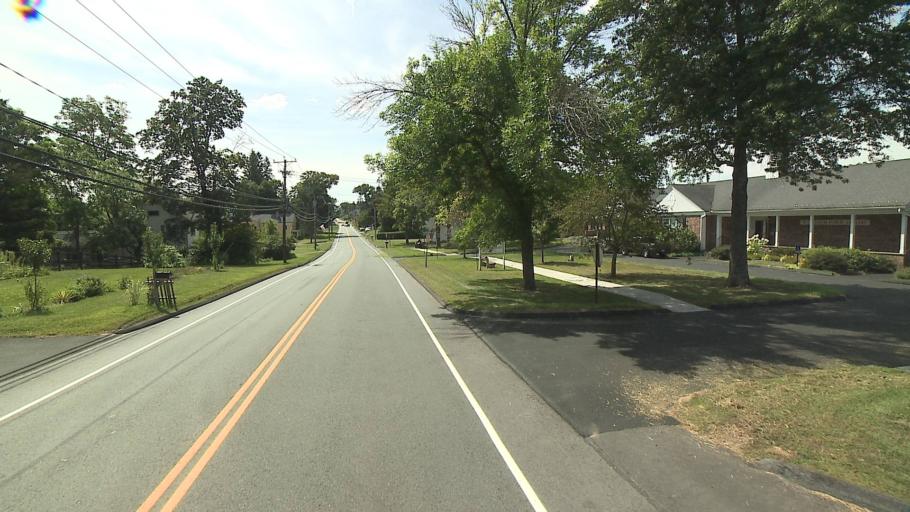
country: US
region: Connecticut
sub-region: Litchfield County
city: Bethlehem Village
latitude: 41.6377
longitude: -73.2087
